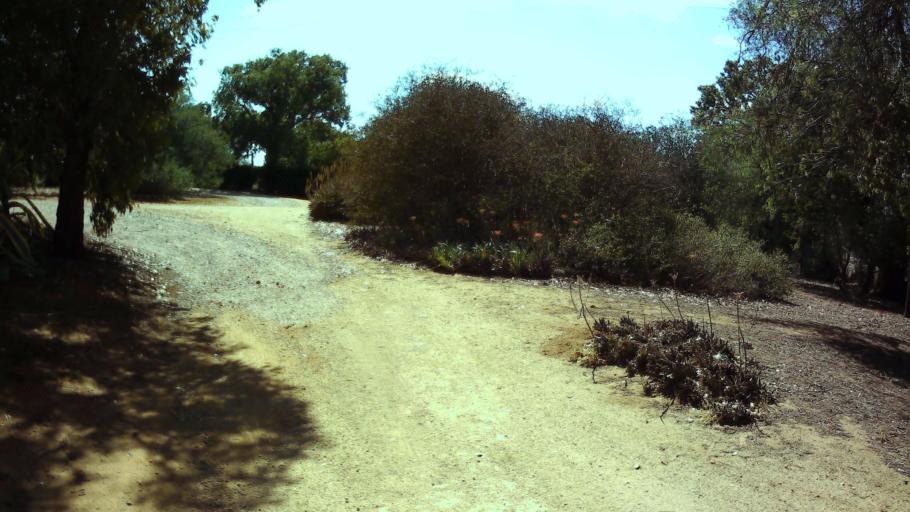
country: AU
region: New South Wales
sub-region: Weddin
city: Grenfell
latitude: -33.9649
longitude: 148.4137
